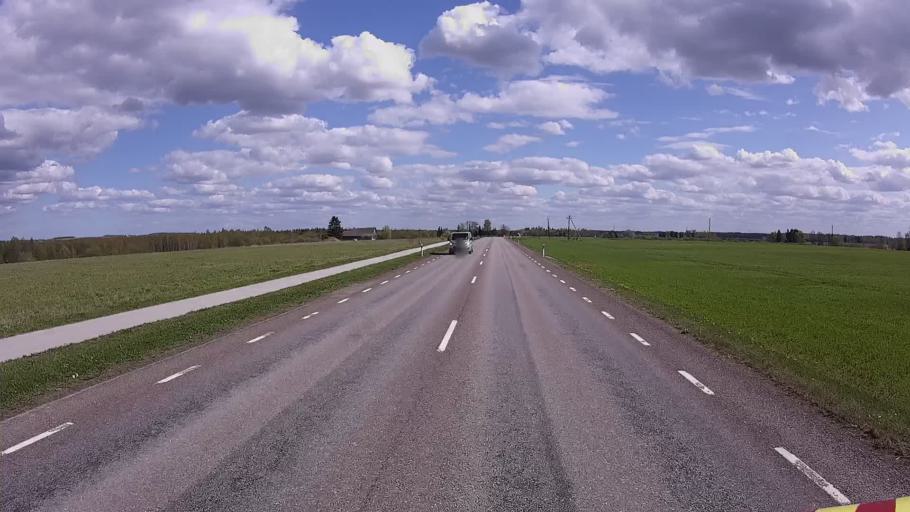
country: EE
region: Jogevamaa
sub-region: Tabivere vald
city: Tabivere
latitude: 58.5414
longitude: 26.6209
